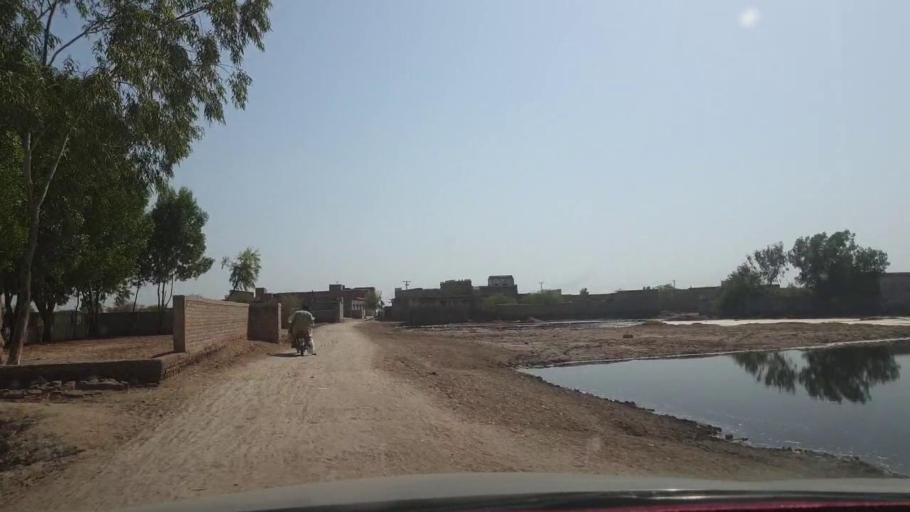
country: PK
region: Sindh
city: Nasirabad
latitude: 27.3467
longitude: 67.8412
